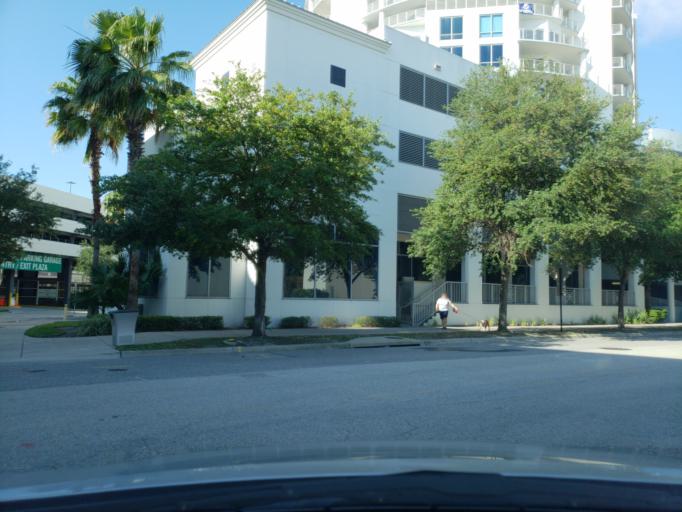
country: US
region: Florida
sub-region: Hillsborough County
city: Tampa
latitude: 27.9451
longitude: -82.4469
